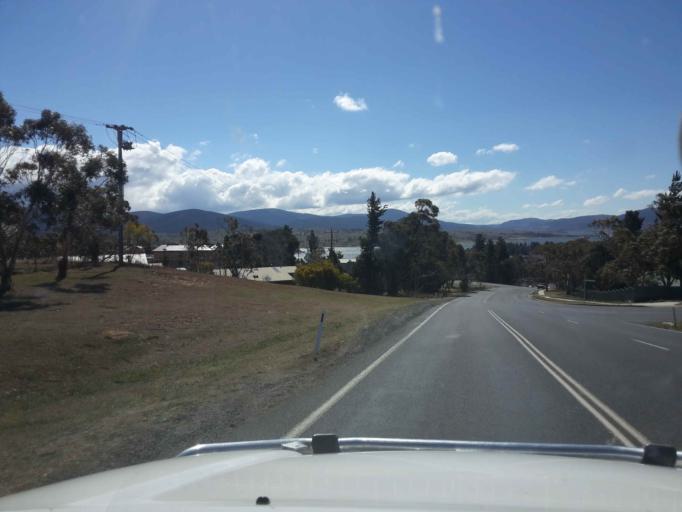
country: AU
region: New South Wales
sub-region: Snowy River
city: Jindabyne
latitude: -36.4196
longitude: 148.6104
